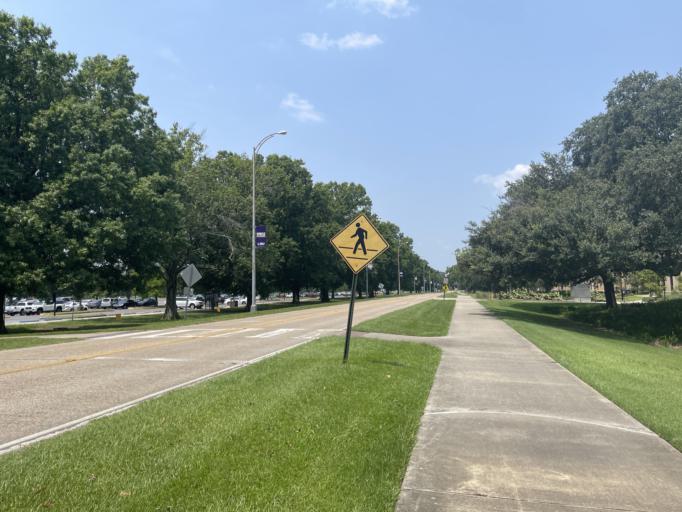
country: US
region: Louisiana
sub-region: East Baton Rouge Parish
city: Baton Rouge
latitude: 30.4065
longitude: -91.1787
